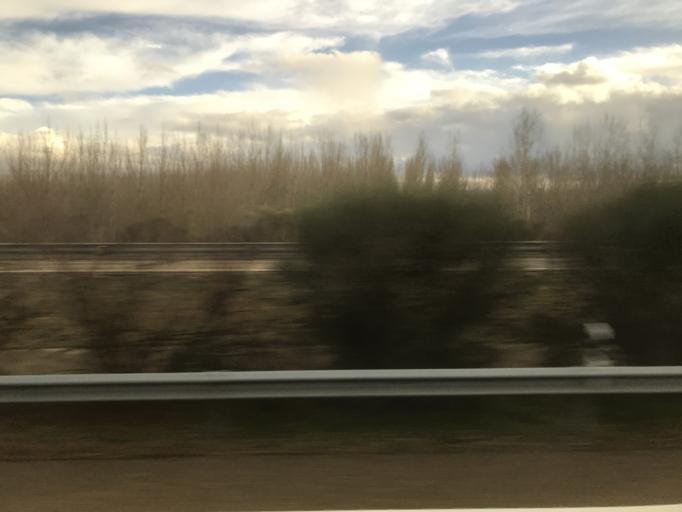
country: ES
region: Castille and Leon
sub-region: Provincia de Palencia
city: Grijota
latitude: 42.0412
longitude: -4.5565
